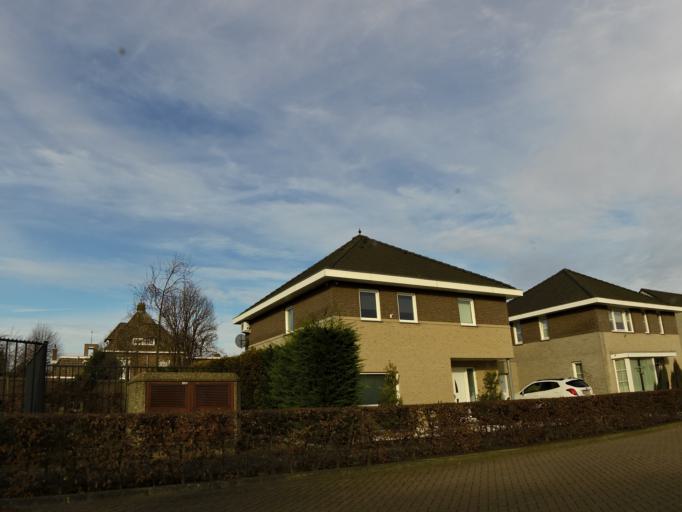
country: NL
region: Limburg
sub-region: Gemeente Heerlen
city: Mariarade
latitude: 50.9303
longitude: 5.9378
